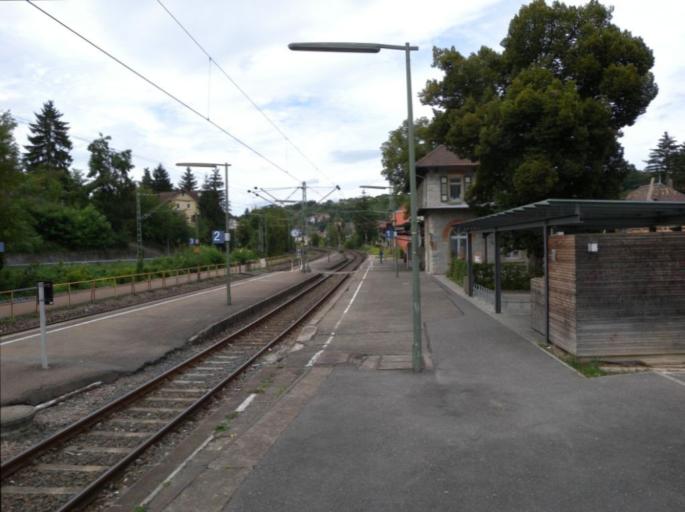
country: DE
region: Baden-Wuerttemberg
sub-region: Regierungsbezirk Stuttgart
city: Mockmuhl
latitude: 49.3208
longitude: 9.3581
